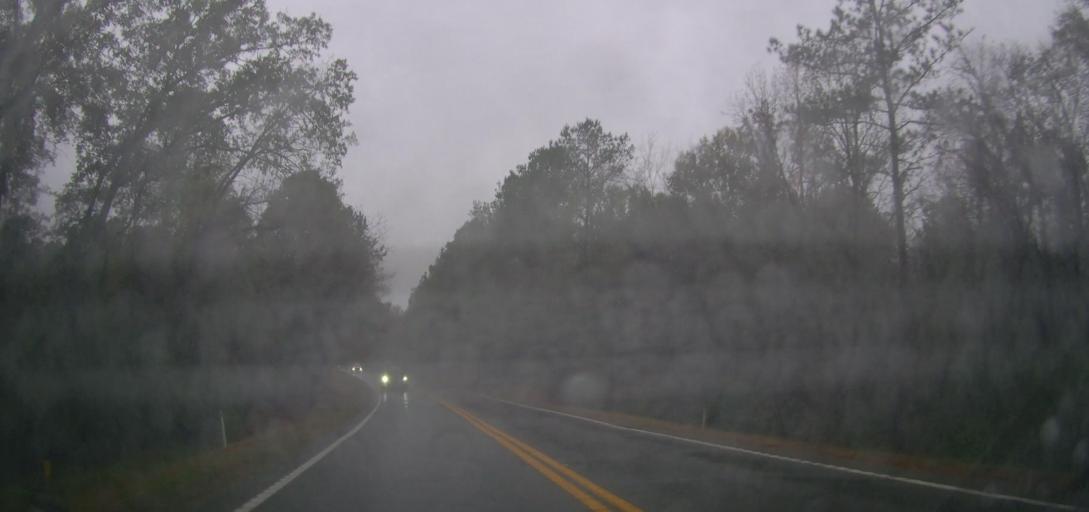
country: US
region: Georgia
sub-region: Jones County
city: Gray
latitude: 33.1511
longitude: -83.4599
